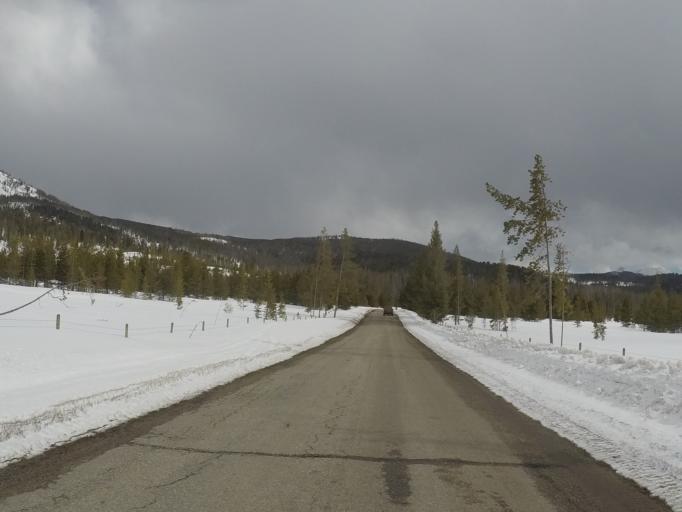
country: US
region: Montana
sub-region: Granite County
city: Philipsburg
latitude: 46.2105
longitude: -113.2539
